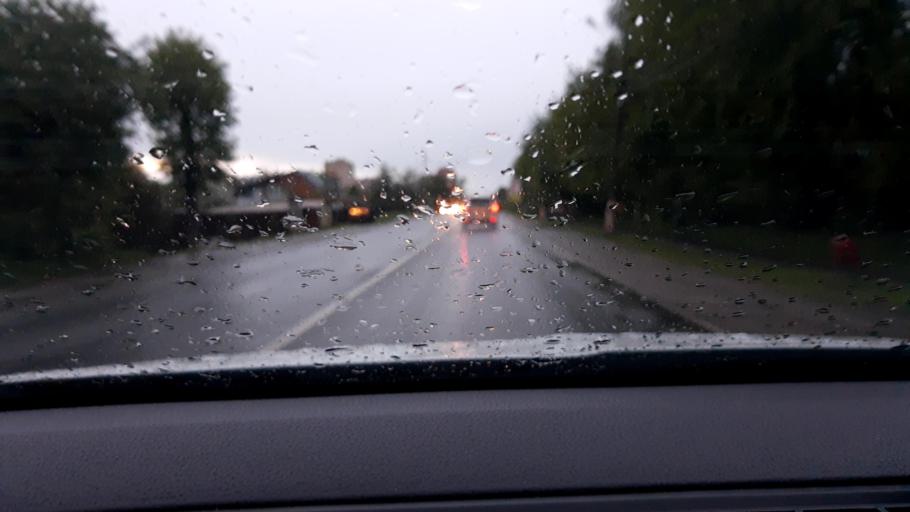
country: RU
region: Moskovskaya
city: Shchelkovo
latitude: 55.9313
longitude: 37.9813
